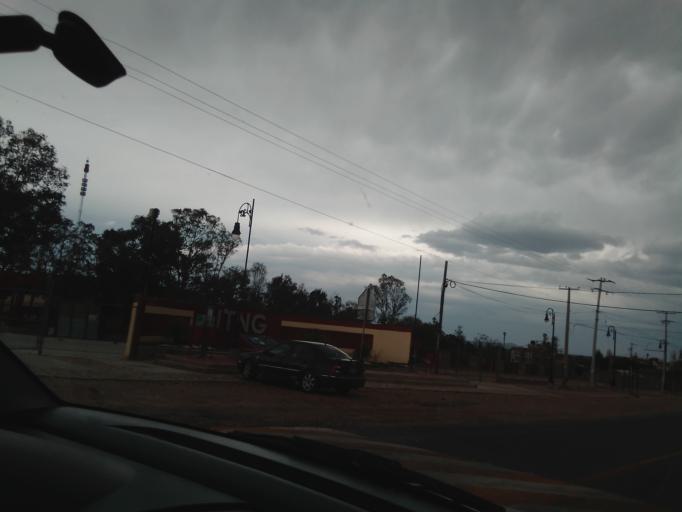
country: MX
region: Guanajuato
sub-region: Dolores Hidalgo Cuna de la Independencia Nacional
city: Colonia Padre Hidalgo
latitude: 21.1680
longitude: -100.9326
